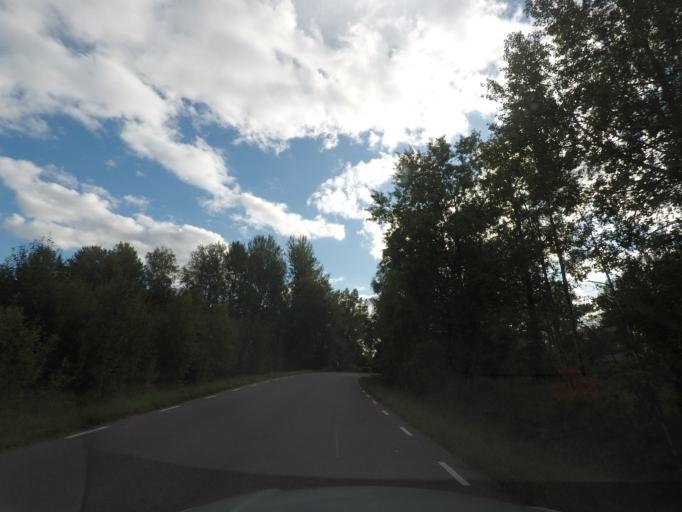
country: SE
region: Vaestmanland
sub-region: Hallstahammars Kommun
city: Kolback
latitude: 59.5215
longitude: 16.1906
